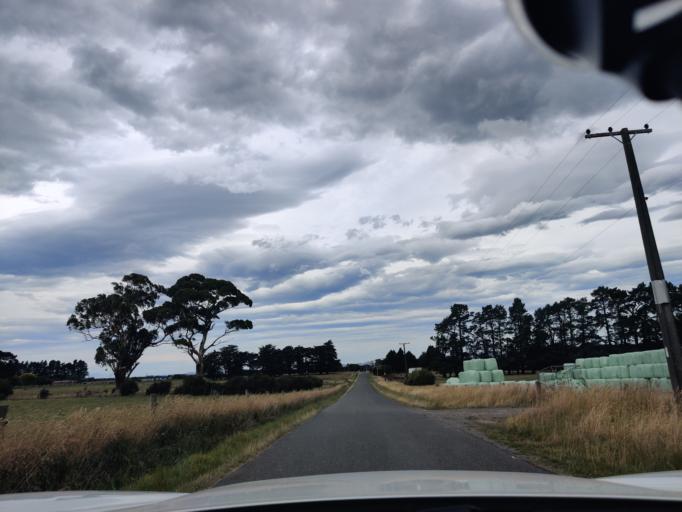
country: NZ
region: Wellington
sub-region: Masterton District
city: Masterton
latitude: -41.0367
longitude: 175.4249
